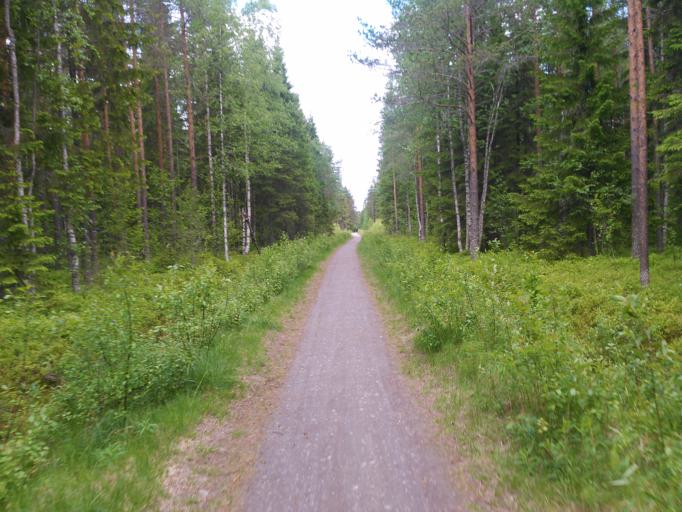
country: SE
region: Vaesterbotten
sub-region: Umea Kommun
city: Ersmark
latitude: 63.8649
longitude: 20.3336
